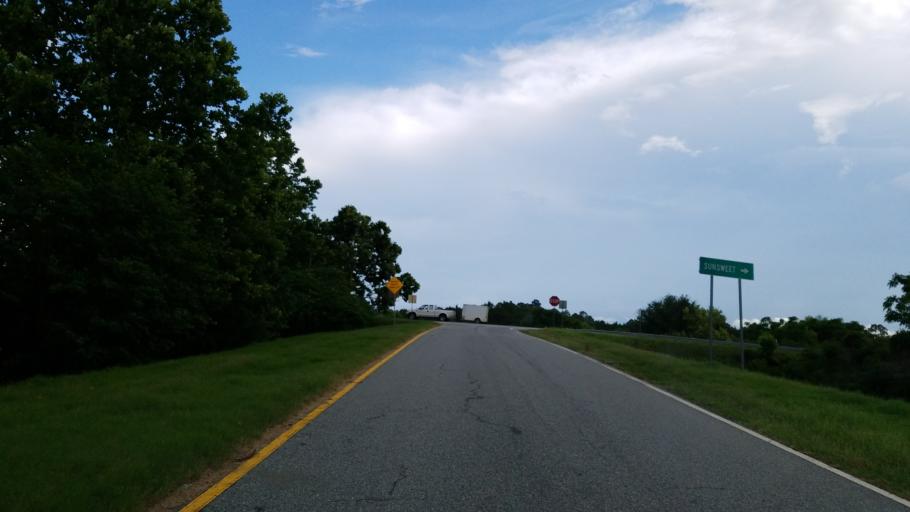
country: US
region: Georgia
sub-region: Tift County
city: Tifton
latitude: 31.5709
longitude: -83.5482
